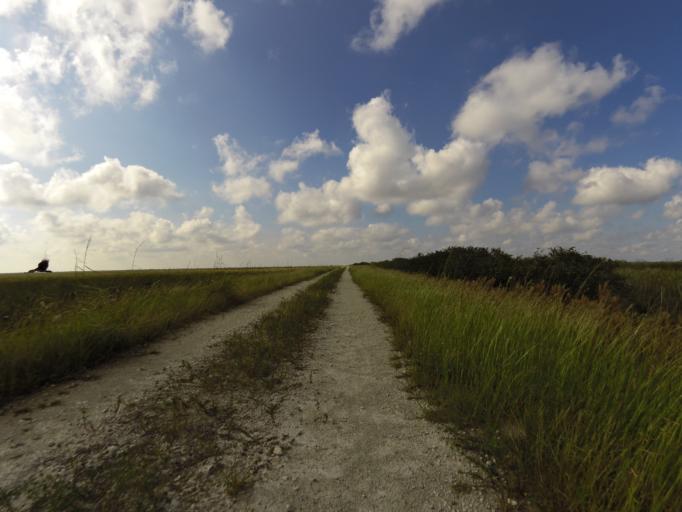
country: US
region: Florida
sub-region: Broward County
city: Weston
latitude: 26.0338
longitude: -80.4931
